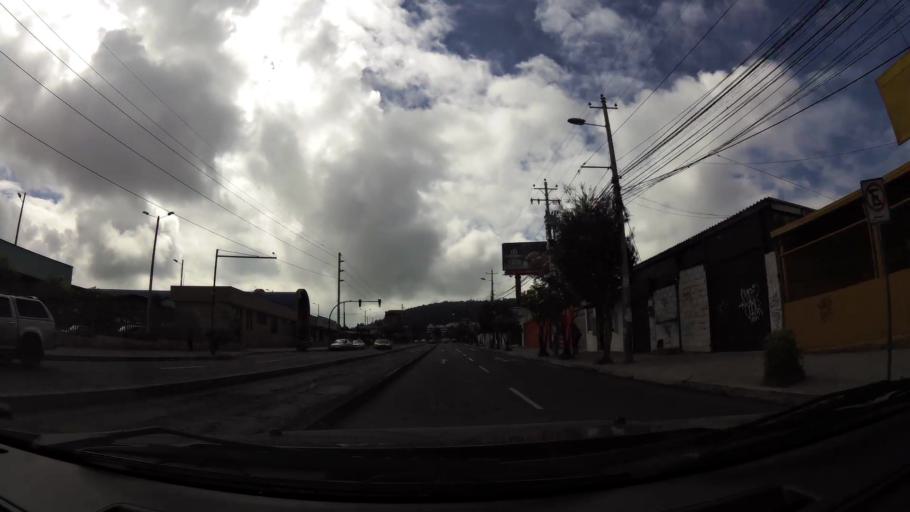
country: EC
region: Pichincha
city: Quito
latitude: -0.1638
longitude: -78.4734
